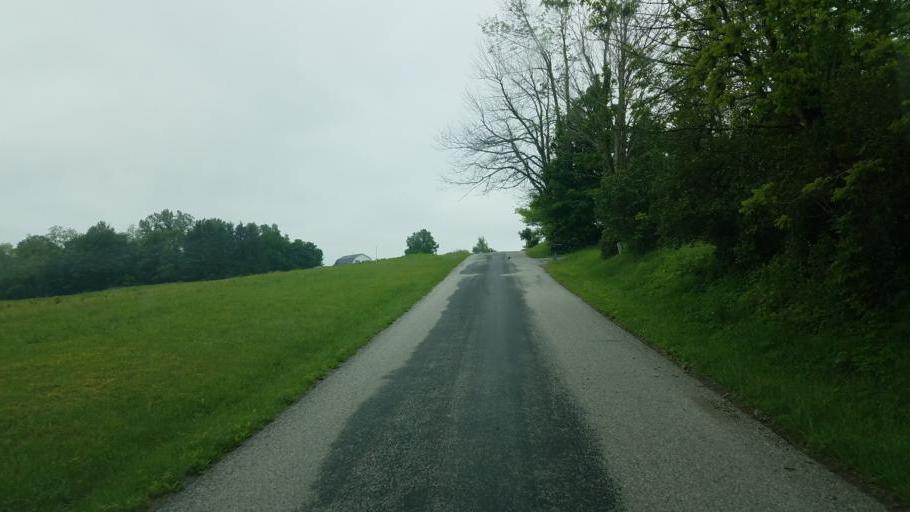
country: US
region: Ohio
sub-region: Knox County
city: Centerburg
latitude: 40.4029
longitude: -82.7316
